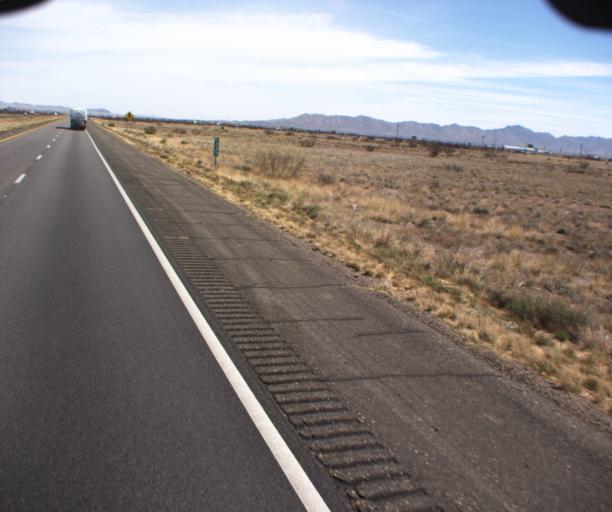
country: US
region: Arizona
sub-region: Cochise County
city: Willcox
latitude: 32.2232
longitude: -109.8773
